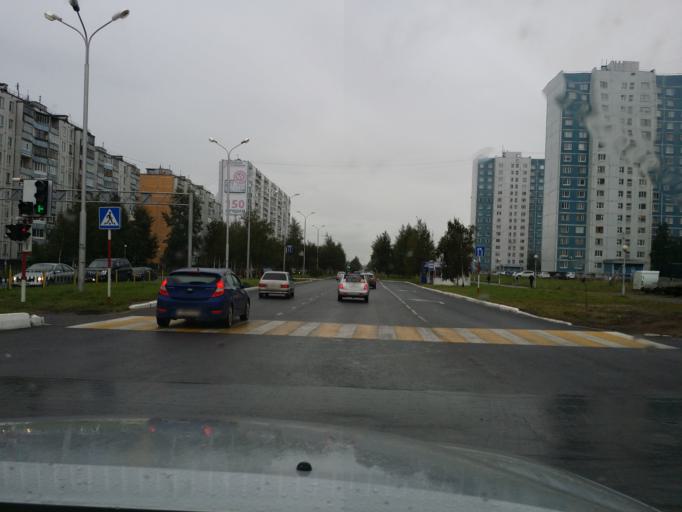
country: RU
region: Khanty-Mansiyskiy Avtonomnyy Okrug
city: Nizhnevartovsk
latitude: 60.9389
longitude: 76.5948
